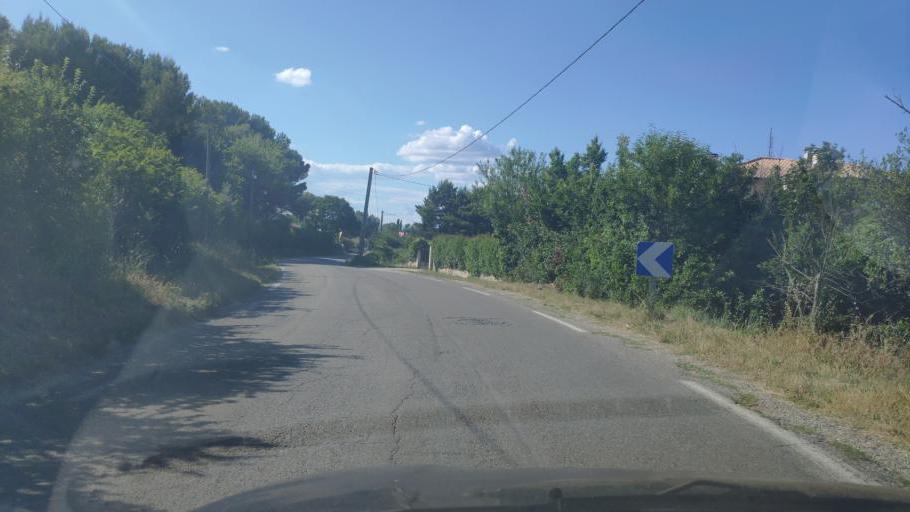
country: FR
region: Provence-Alpes-Cote d'Azur
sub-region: Departement du Vaucluse
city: Entraigues-sur-la-Sorgue
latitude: 43.9893
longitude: 4.9146
